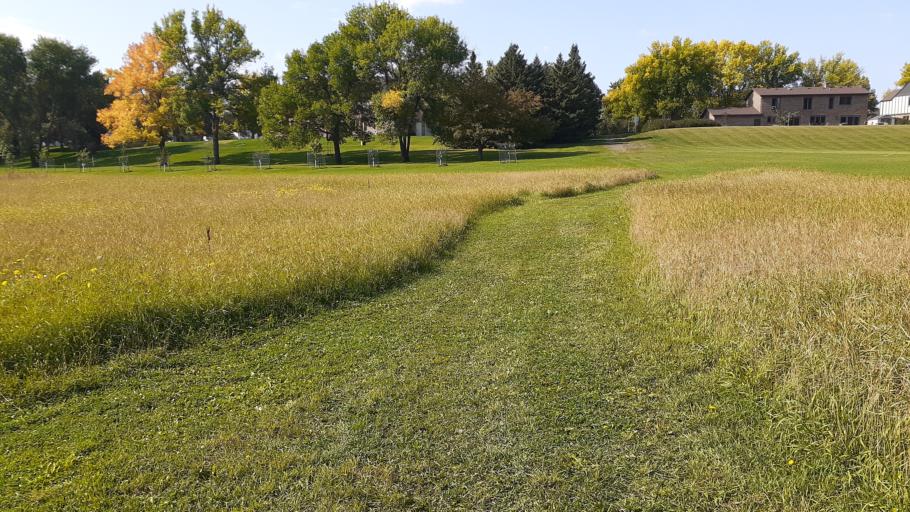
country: US
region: Minnesota
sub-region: Clay County
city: Oakport
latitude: 46.9110
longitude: -96.7652
